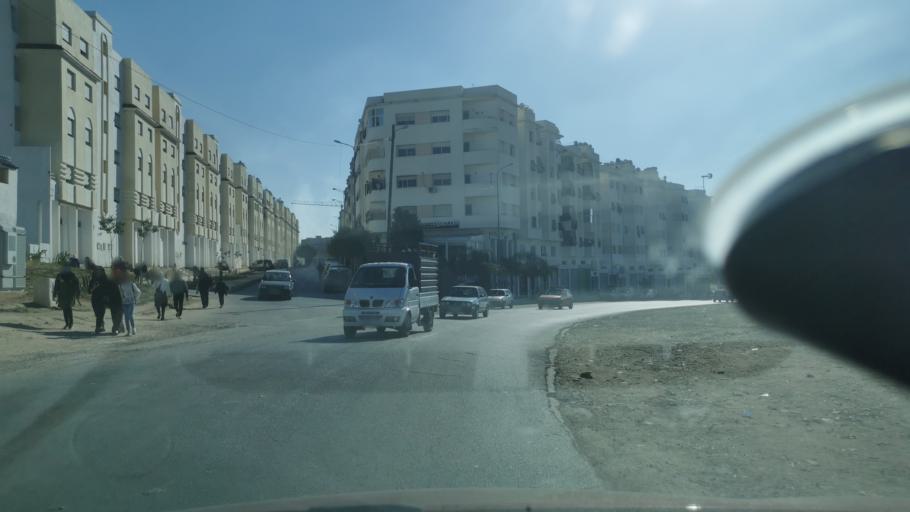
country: MA
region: Fes-Boulemane
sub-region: Fes
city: Fes
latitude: 34.0389
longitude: -4.9890
